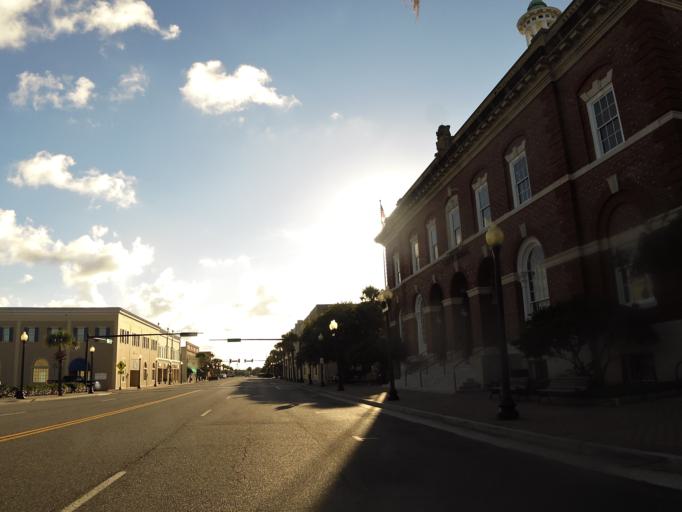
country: US
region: Georgia
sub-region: Glynn County
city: Brunswick
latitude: 31.1496
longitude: -81.4935
